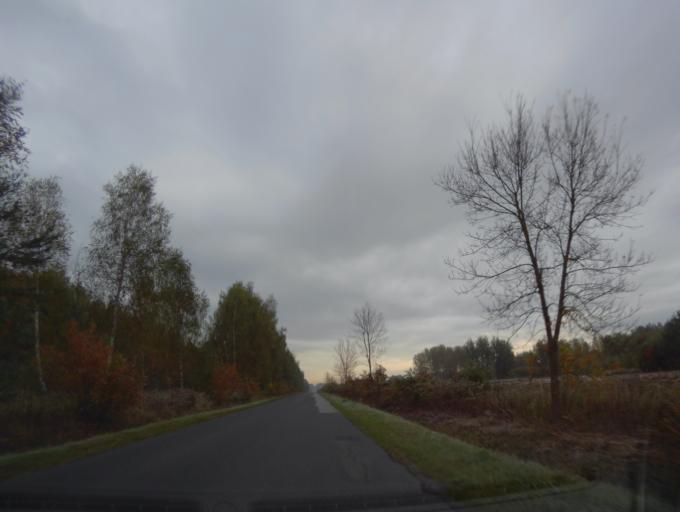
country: PL
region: Subcarpathian Voivodeship
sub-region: Powiat nizanski
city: Krzeszow
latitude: 50.4339
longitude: 22.3757
